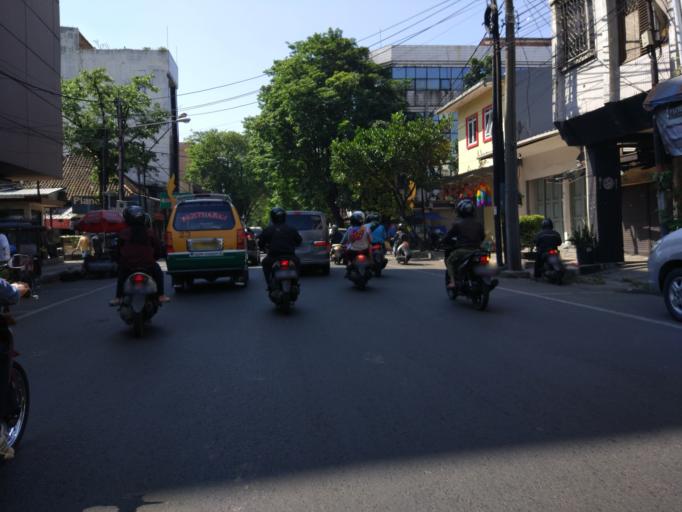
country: ID
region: West Java
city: Bandung
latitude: -6.9269
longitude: 107.6003
